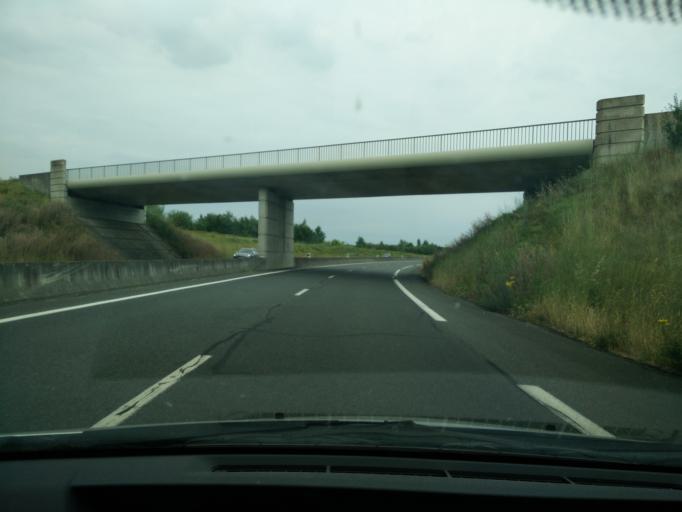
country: FR
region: Pays de la Loire
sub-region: Departement de Maine-et-Loire
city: Doue-la-Fontaine
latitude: 47.1934
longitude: -0.3173
